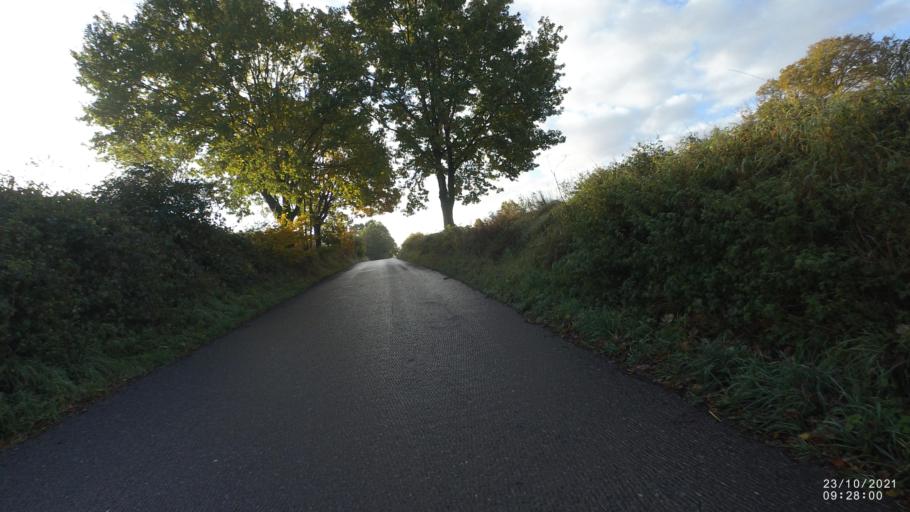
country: DE
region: North Rhine-Westphalia
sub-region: Regierungsbezirk Arnsberg
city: Menden
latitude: 51.4534
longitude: 7.8015
